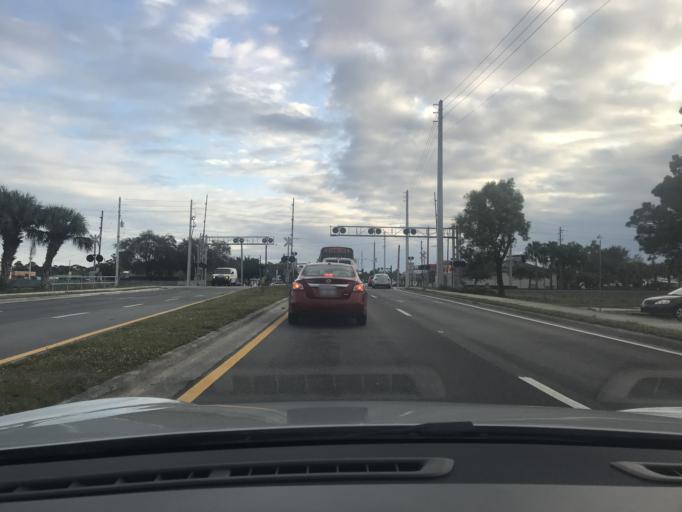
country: US
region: Florida
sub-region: Martin County
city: Port Salerno
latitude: 27.1673
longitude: -80.2235
